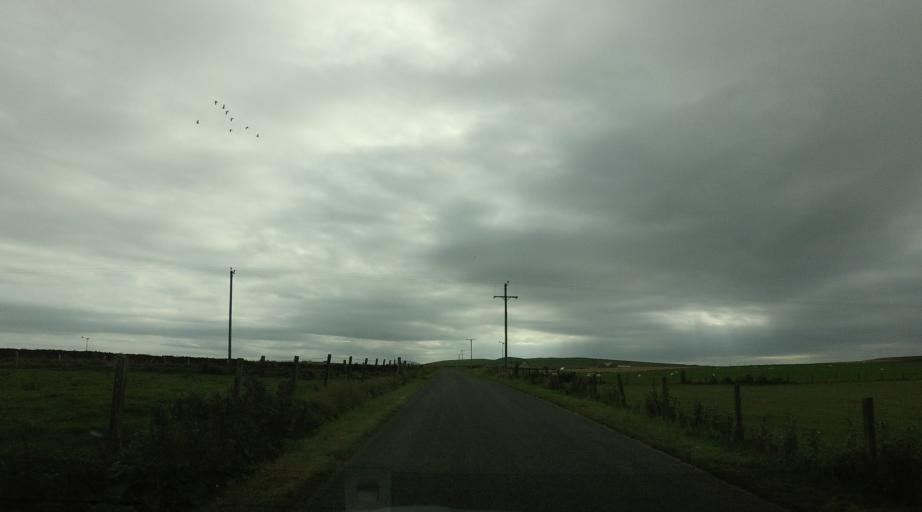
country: GB
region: Scotland
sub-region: Orkney Islands
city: Stromness
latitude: 59.0370
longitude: -3.3117
